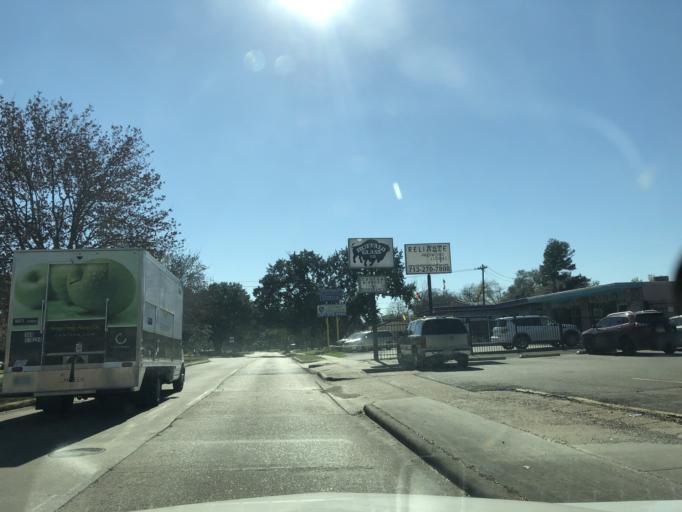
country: US
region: Texas
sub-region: Harris County
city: Bellaire
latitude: 29.6928
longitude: -95.4931
